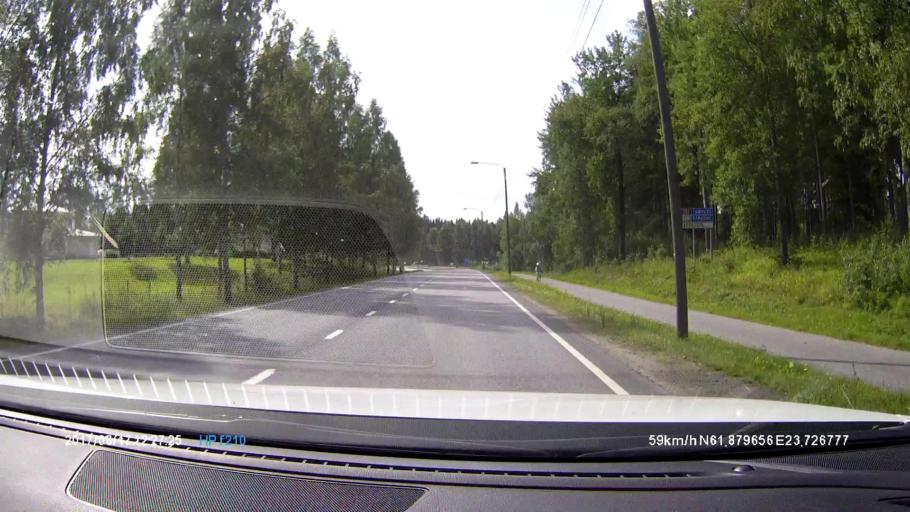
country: FI
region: Pirkanmaa
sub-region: Tampere
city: Kuru
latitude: 61.8793
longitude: 23.7265
